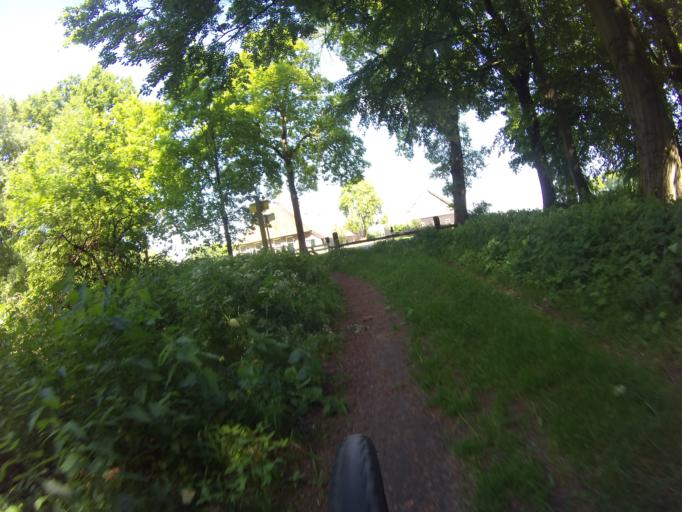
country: NL
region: Drenthe
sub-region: Gemeente Coevorden
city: Sleen
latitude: 52.7582
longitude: 6.7472
